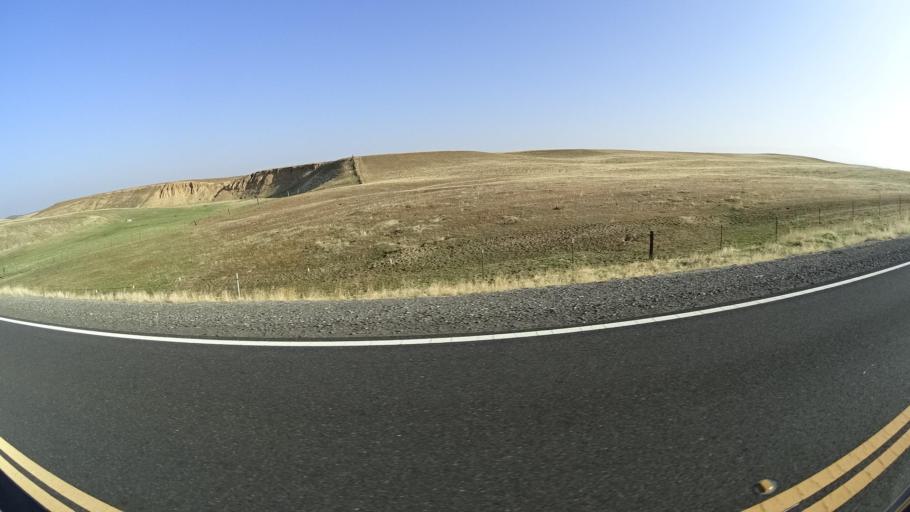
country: US
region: California
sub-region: Tulare County
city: Richgrove
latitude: 35.7466
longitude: -118.9822
